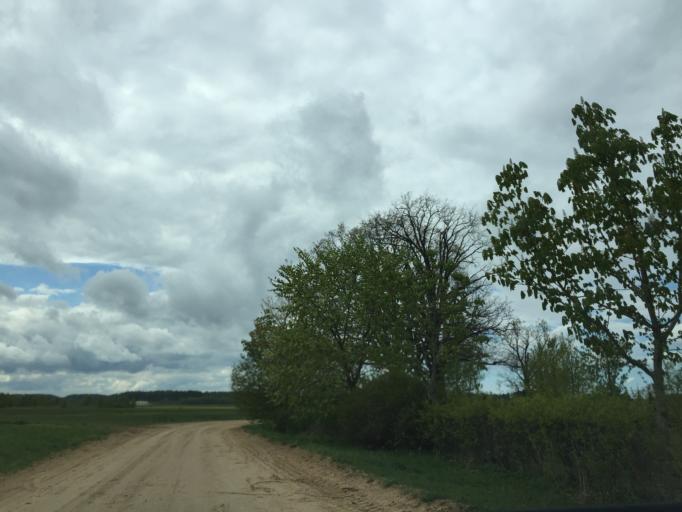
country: LV
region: Kekava
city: Kekava
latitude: 56.8094
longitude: 24.2979
